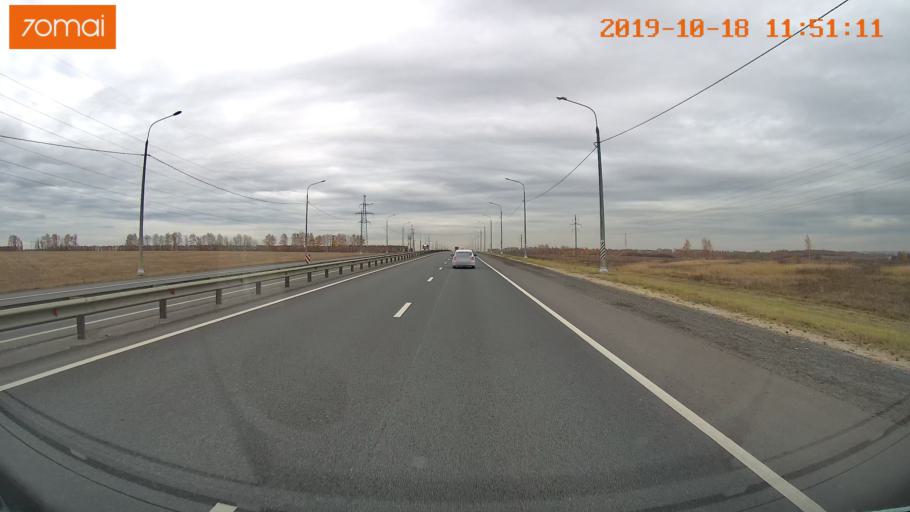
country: RU
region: Rjazan
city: Mikhaylov
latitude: 54.2582
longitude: 39.0169
